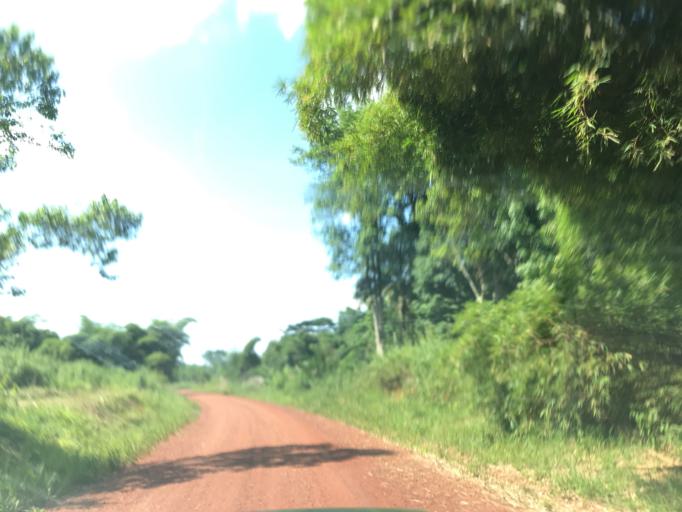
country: CD
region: Eastern Province
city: Kisangani
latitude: 1.2310
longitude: 25.2705
